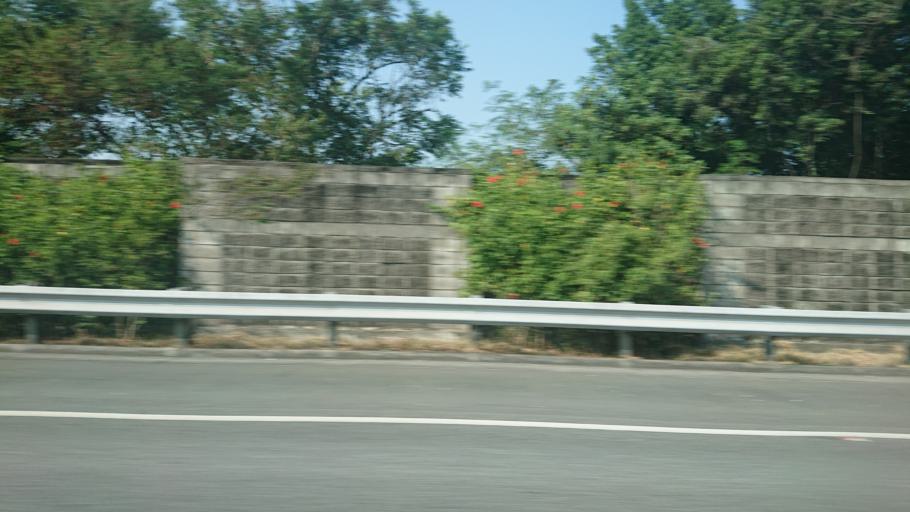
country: TW
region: Taiwan
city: Lugu
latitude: 23.7869
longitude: 120.7045
